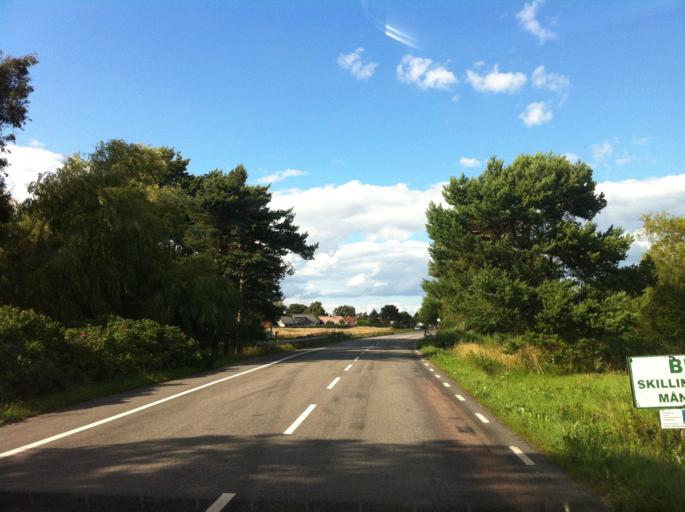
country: SE
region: Skane
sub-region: Simrishamns Kommun
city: Simrishamn
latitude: 55.4585
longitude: 14.2720
